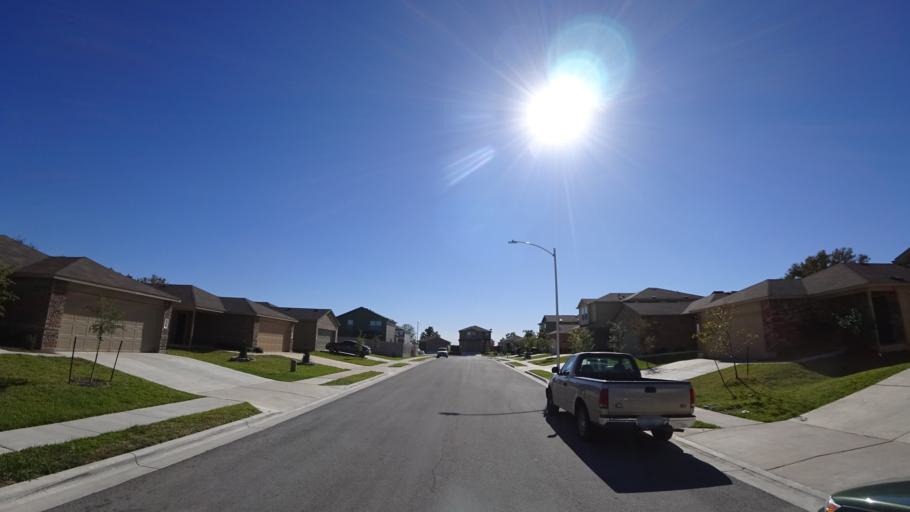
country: US
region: Texas
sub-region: Travis County
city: Hornsby Bend
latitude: 30.2782
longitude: -97.6252
